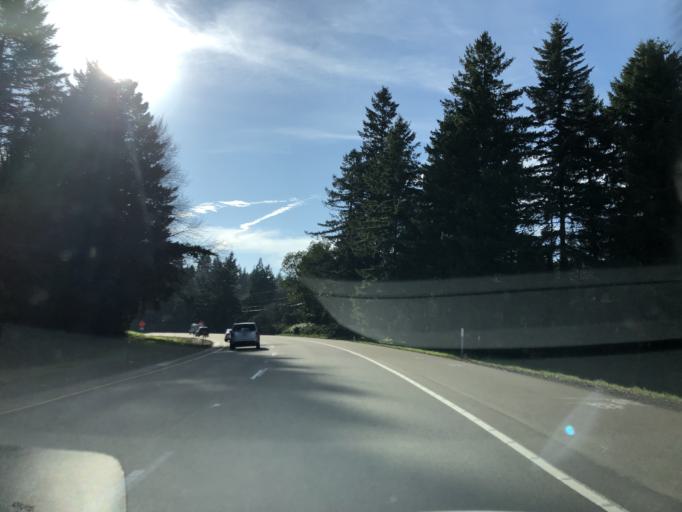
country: US
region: Oregon
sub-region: Washington County
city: Tualatin
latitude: 45.3722
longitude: -122.7585
